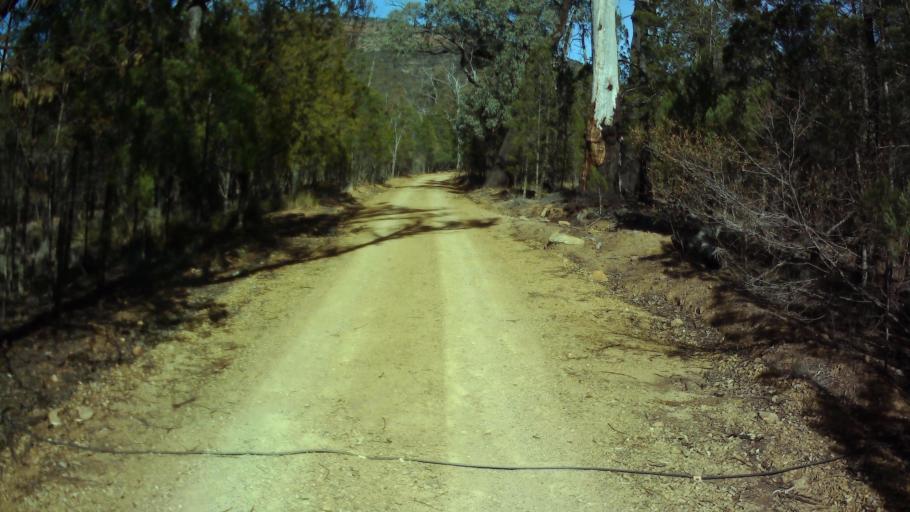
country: AU
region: New South Wales
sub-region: Weddin
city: Grenfell
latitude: -33.8983
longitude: 148.0049
